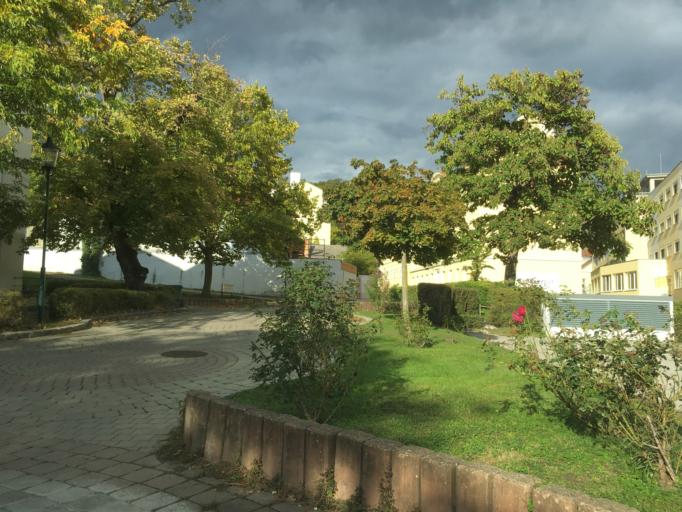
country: AT
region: Lower Austria
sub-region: Politischer Bezirk Baden
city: Baden
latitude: 48.0085
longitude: 16.2277
